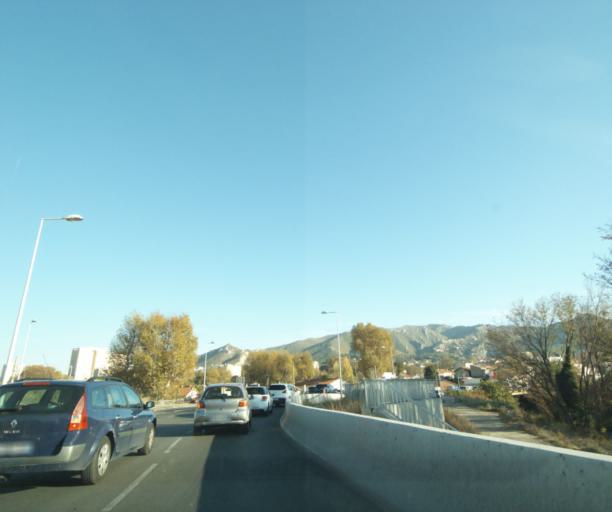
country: FR
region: Provence-Alpes-Cote d'Azur
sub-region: Departement des Bouches-du-Rhone
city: Marseille 10
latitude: 43.2846
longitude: 5.4259
